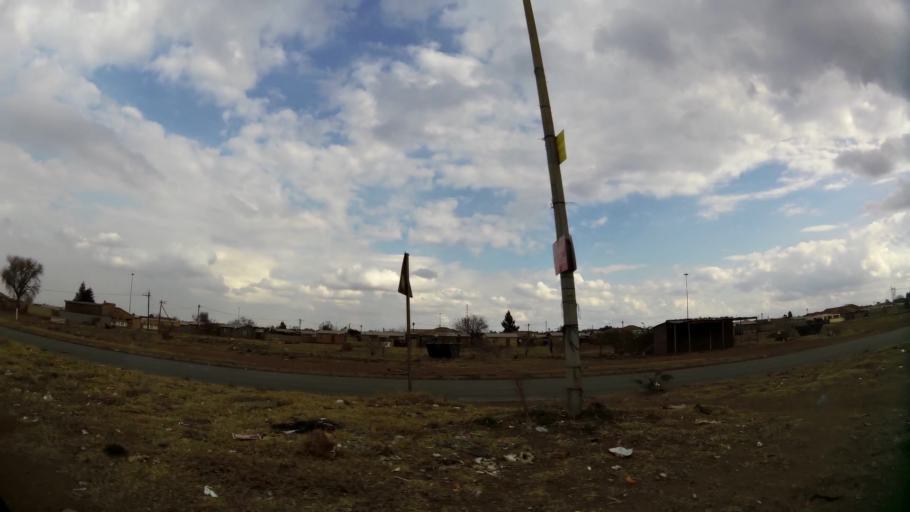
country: ZA
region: Gauteng
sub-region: Sedibeng District Municipality
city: Vanderbijlpark
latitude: -26.6608
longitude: 27.8482
